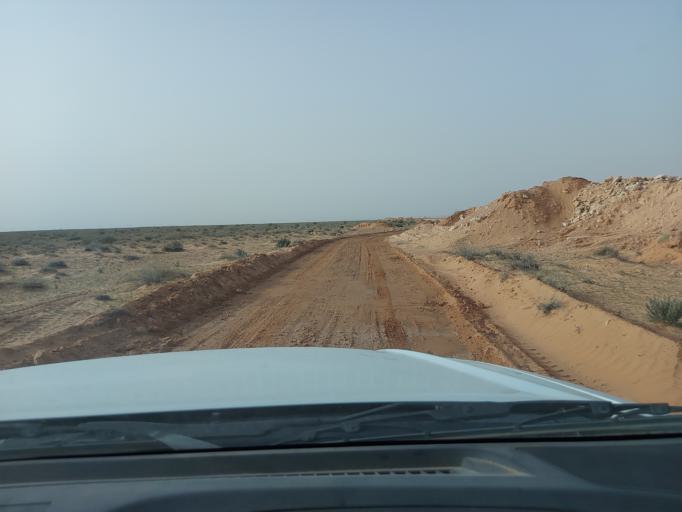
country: TN
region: Madanin
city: Medenine
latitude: 33.2777
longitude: 10.5929
